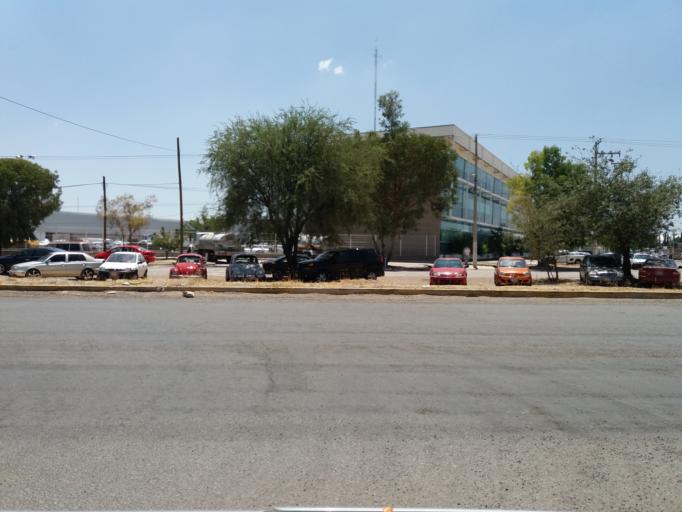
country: MX
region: Aguascalientes
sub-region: Aguascalientes
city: San Sebastian [Fraccionamiento]
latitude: 21.8003
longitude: -102.2895
